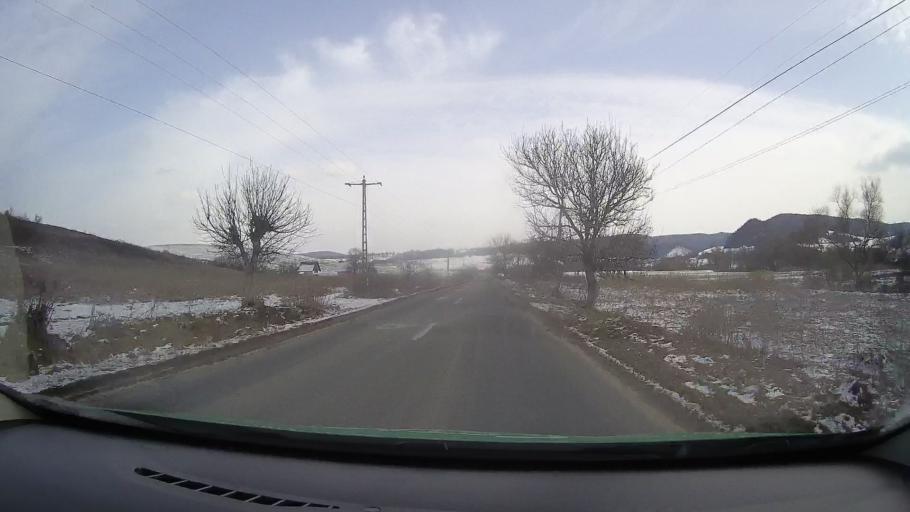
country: RO
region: Mures
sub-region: Comuna Apold
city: Saes
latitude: 46.1445
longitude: 24.7796
